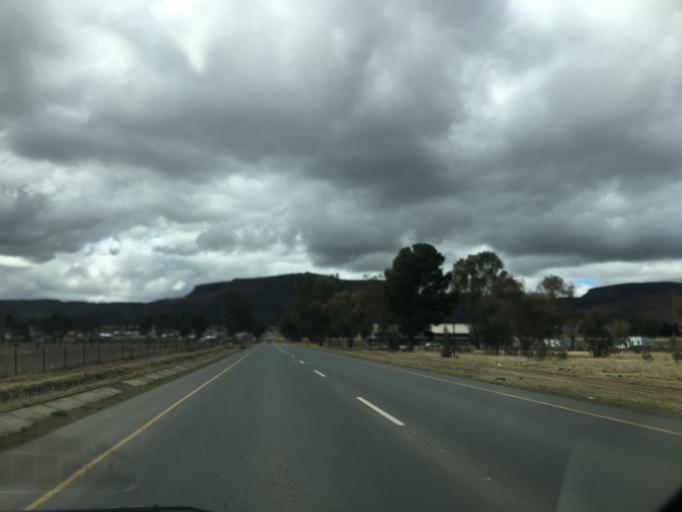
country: ZA
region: Eastern Cape
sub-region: Chris Hani District Municipality
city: Cala
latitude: -31.5301
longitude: 27.6779
